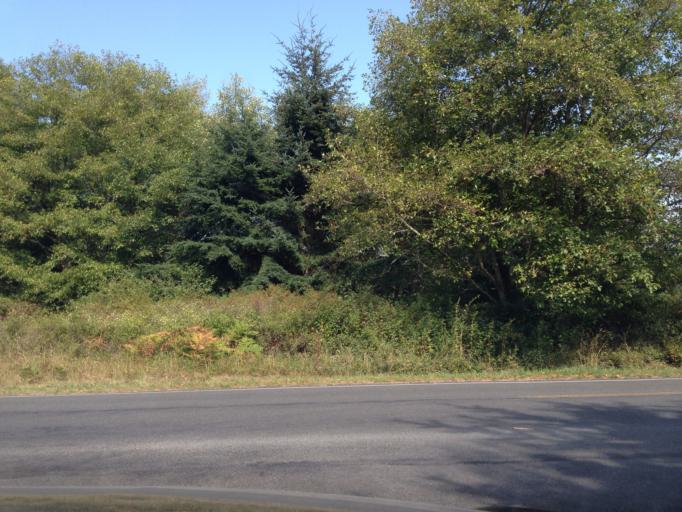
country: US
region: Washington
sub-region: San Juan County
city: Friday Harbor
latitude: 48.4652
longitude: -123.0278
